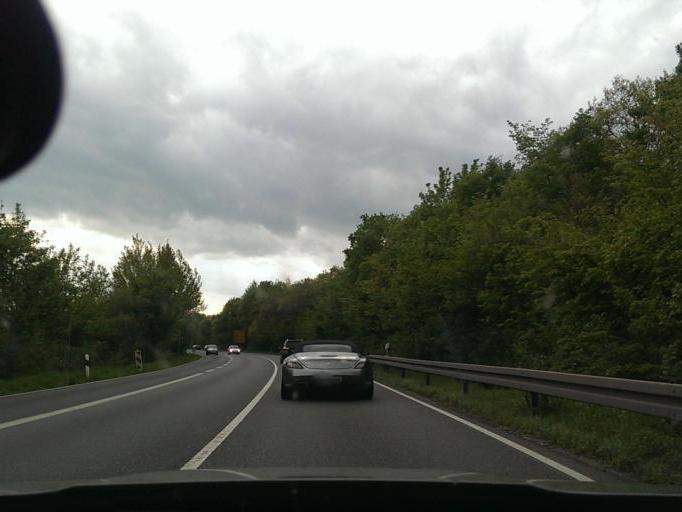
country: DE
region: Lower Saxony
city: Laatzen
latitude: 52.2993
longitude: 9.8244
